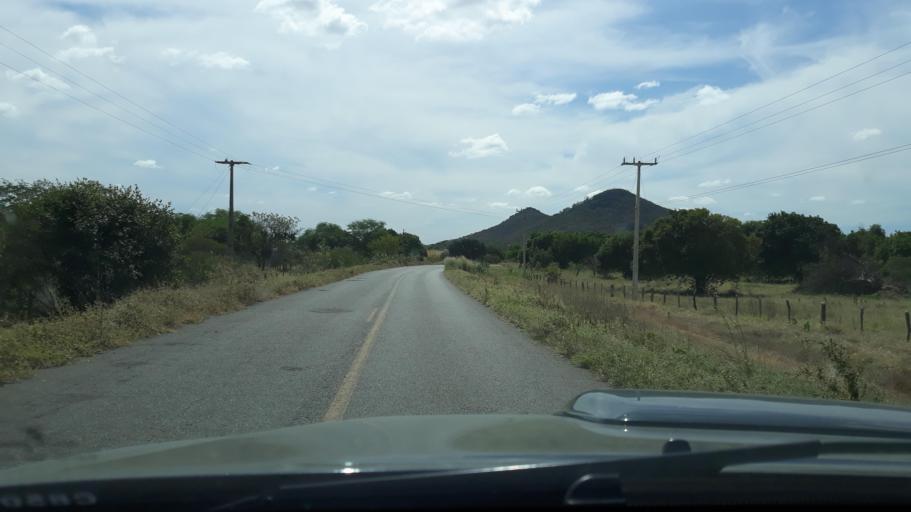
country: BR
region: Bahia
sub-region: Guanambi
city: Guanambi
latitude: -14.0759
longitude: -42.8791
